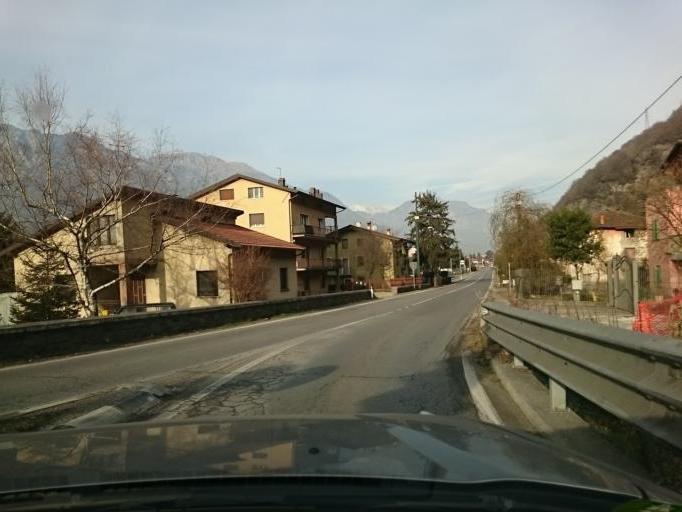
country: IT
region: Lombardy
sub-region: Provincia di Brescia
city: Gratacasolo
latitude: 45.8189
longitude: 10.1224
